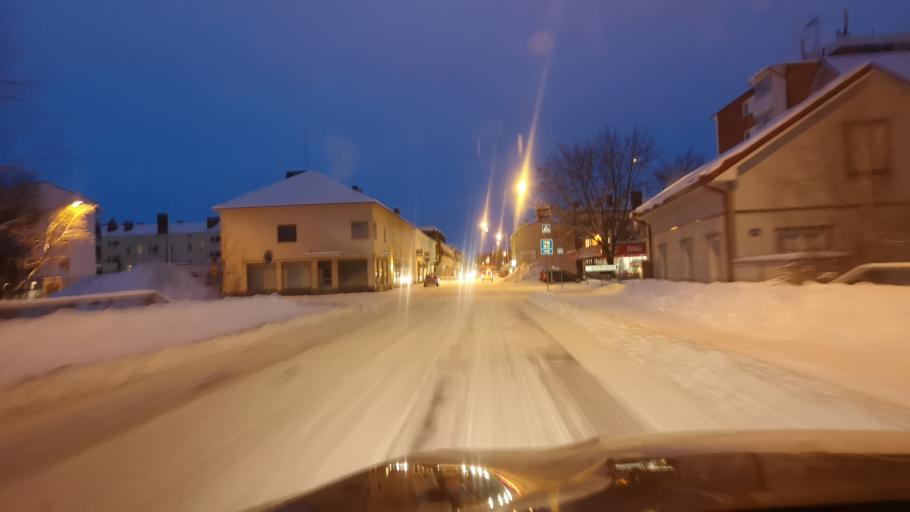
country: FI
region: Varsinais-Suomi
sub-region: Loimaa
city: Loimaa
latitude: 60.8524
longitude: 23.0614
